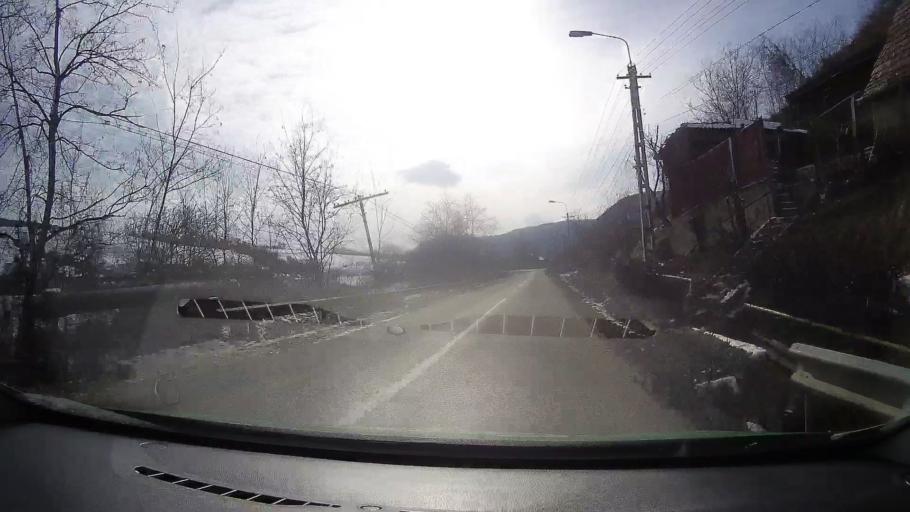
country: RO
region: Mures
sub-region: Municipiul Sighisoara
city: Sighisoara
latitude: 46.2052
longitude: 24.7776
